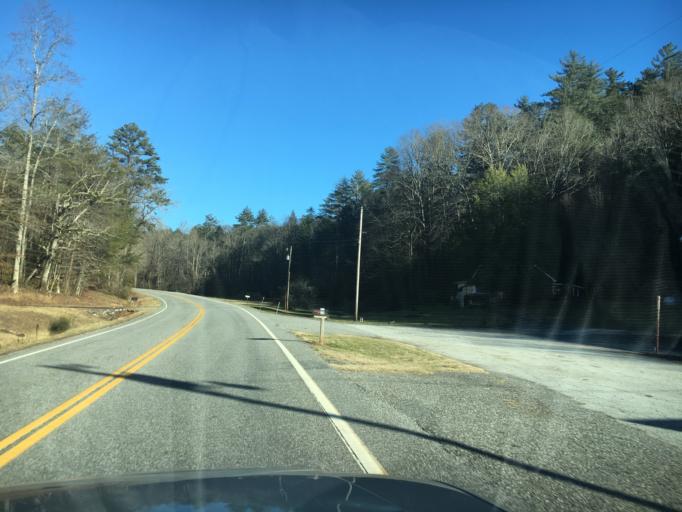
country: US
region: Georgia
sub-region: White County
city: Cleveland
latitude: 34.6609
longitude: -83.8948
